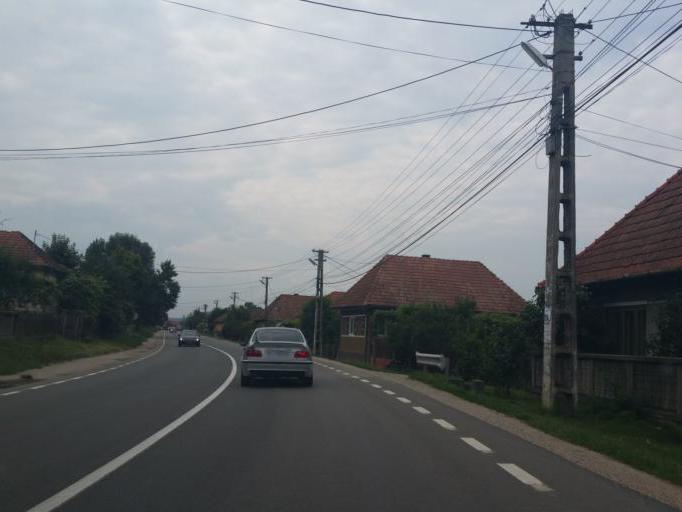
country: RO
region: Salaj
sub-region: Comuna Hida
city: Hida
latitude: 47.0383
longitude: 23.2654
